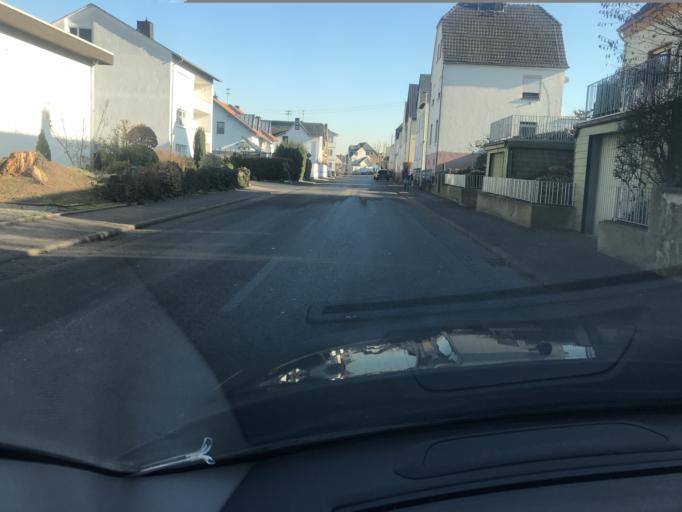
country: DE
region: Hesse
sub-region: Regierungsbezirk Giessen
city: Elz
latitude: 50.4114
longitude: 8.0266
